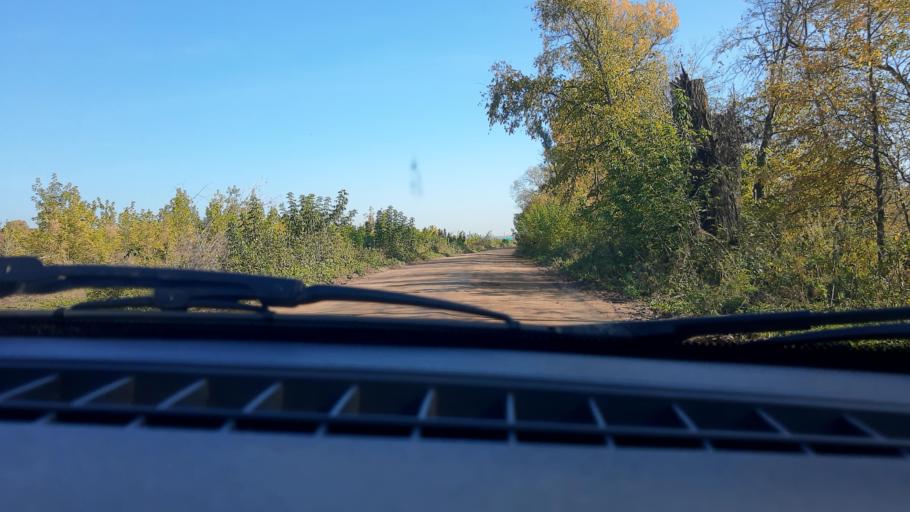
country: RU
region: Bashkortostan
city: Mikhaylovka
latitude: 54.7480
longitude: 55.8704
